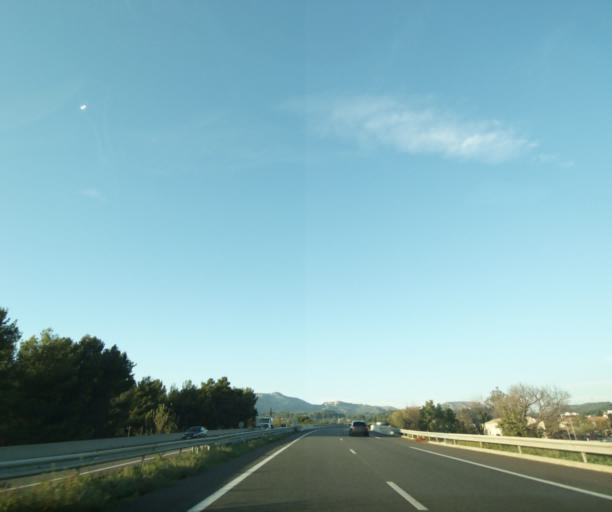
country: FR
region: Provence-Alpes-Cote d'Azur
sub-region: Departement des Bouches-du-Rhone
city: Aubagne
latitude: 43.3156
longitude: 5.5907
